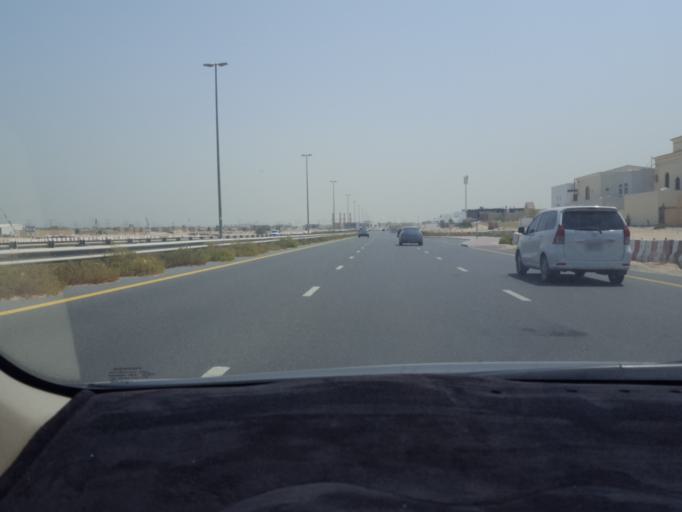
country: AE
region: Dubai
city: Dubai
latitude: 25.0776
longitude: 55.2234
